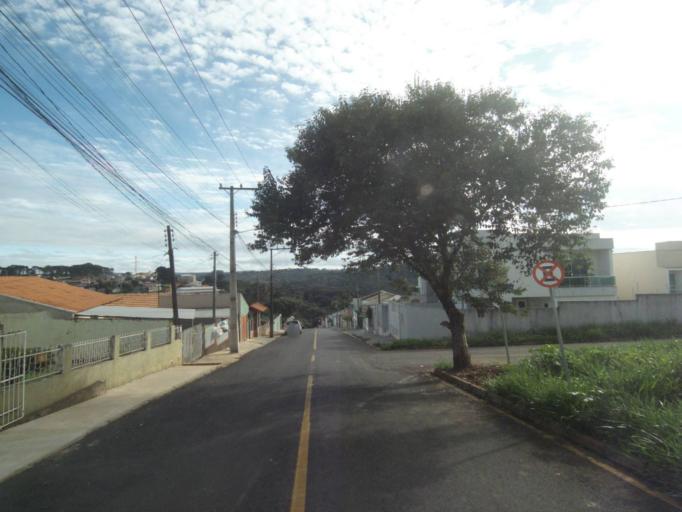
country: BR
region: Parana
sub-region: Telemaco Borba
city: Telemaco Borba
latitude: -24.3385
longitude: -50.6103
